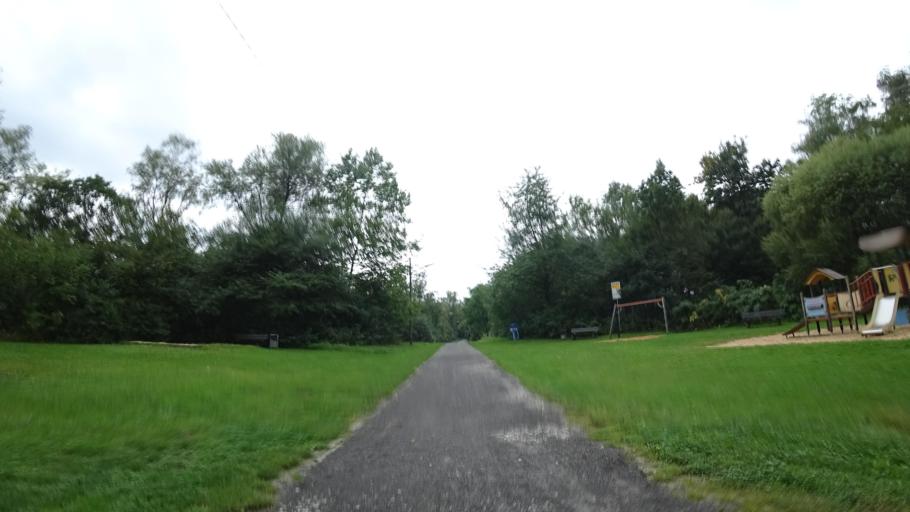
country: DE
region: North Rhine-Westphalia
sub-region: Regierungsbezirk Detmold
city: Bielefeld
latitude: 52.0442
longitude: 8.5521
